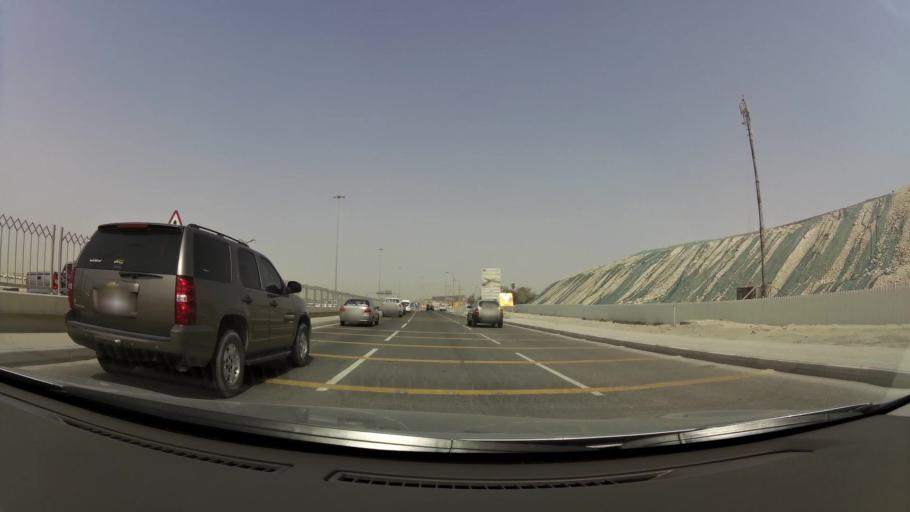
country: QA
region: Baladiyat ad Dawhah
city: Doha
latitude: 25.2881
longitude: 51.4804
